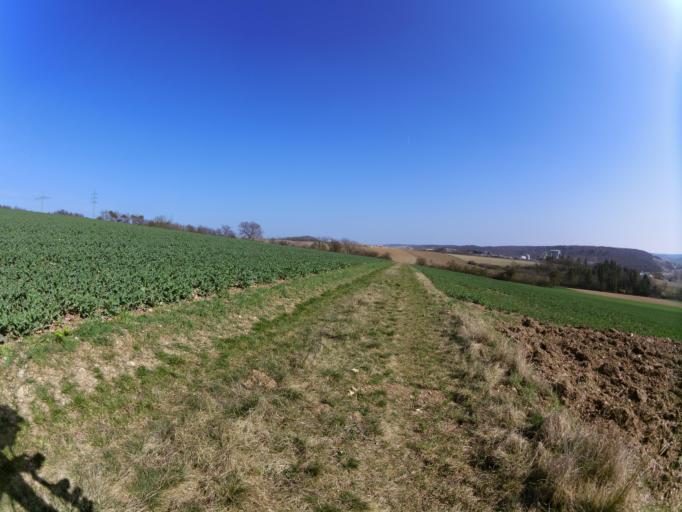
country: DE
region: Bavaria
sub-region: Regierungsbezirk Unterfranken
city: Greussenheim
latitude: 49.8037
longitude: 9.7584
